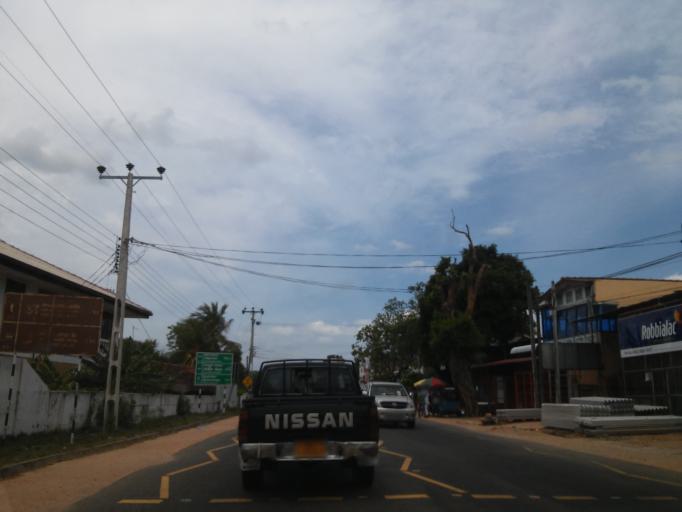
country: LK
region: Eastern Province
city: Trincomalee
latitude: 8.5876
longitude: 81.2050
